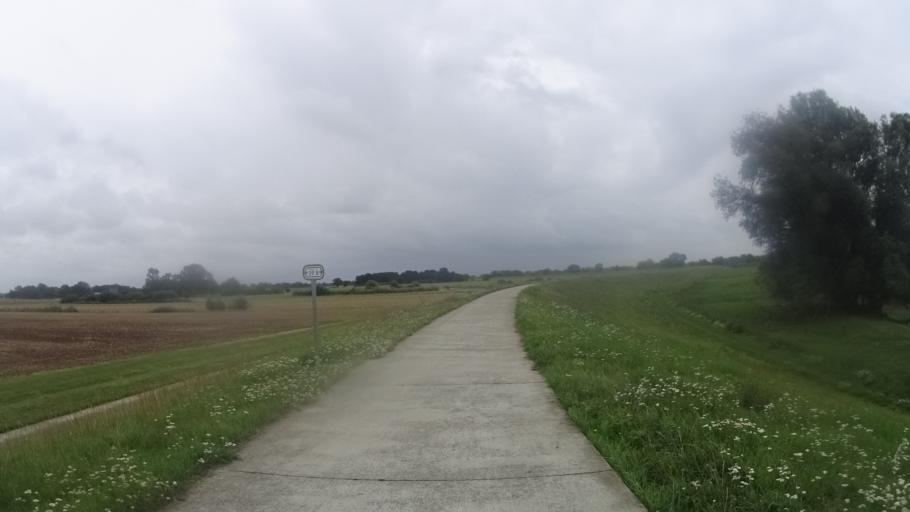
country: DE
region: Lower Saxony
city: Bleckede
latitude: 53.2979
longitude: 10.7581
